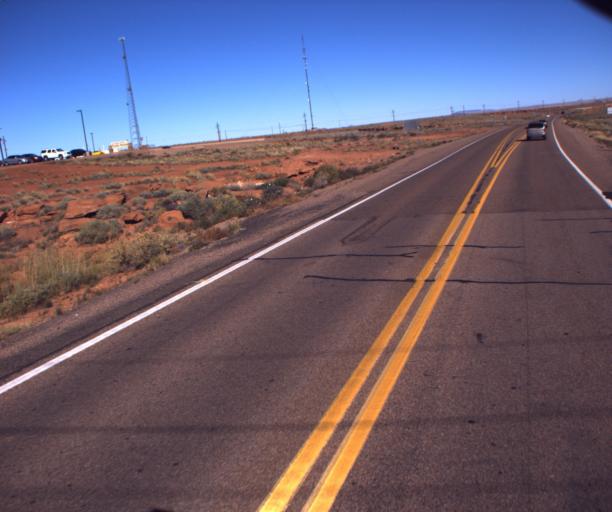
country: US
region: Arizona
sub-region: Navajo County
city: Holbrook
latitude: 34.8704
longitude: -110.1608
